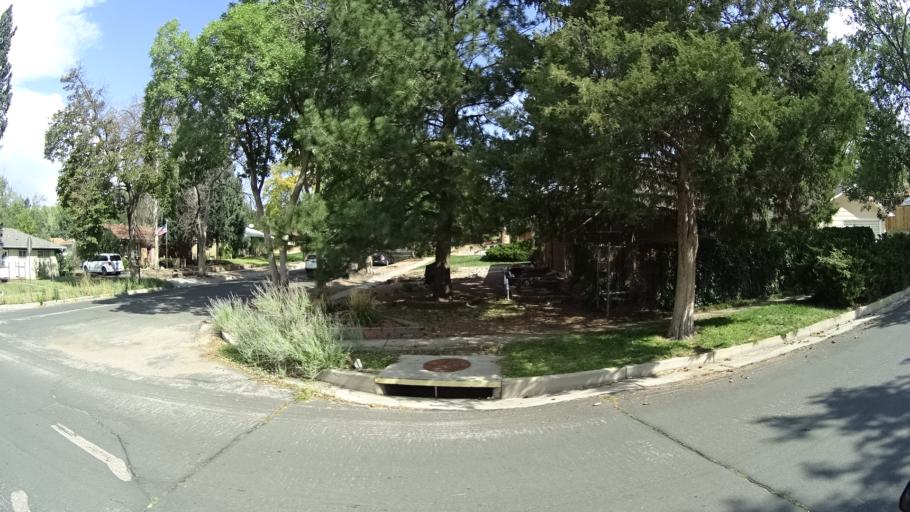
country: US
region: Colorado
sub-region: El Paso County
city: Colorado Springs
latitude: 38.8626
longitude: -104.7732
